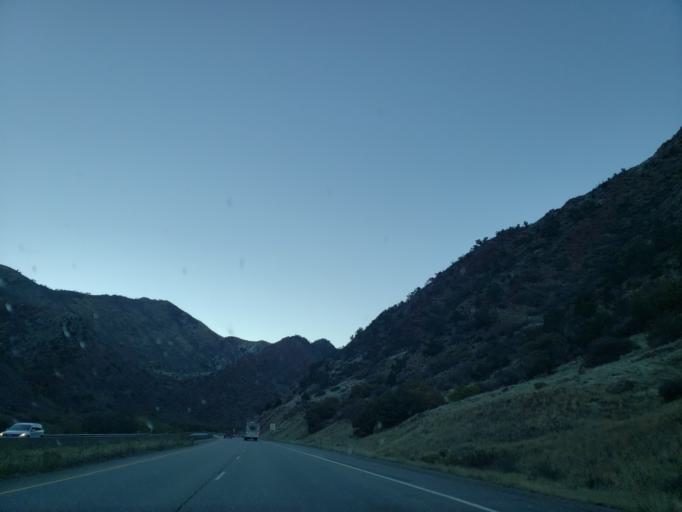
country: US
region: Colorado
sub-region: Garfield County
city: Glenwood Springs
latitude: 39.5658
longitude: -107.4171
